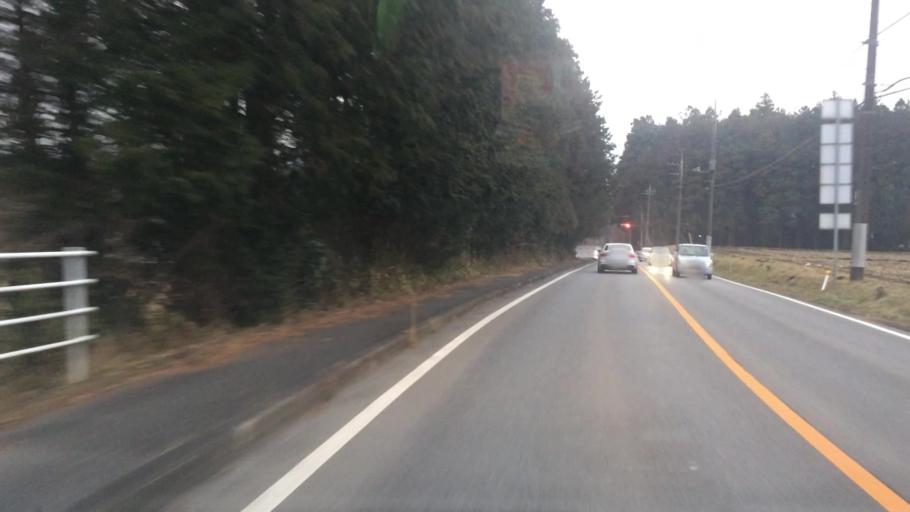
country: JP
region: Tochigi
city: Imaichi
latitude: 36.6691
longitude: 139.7754
